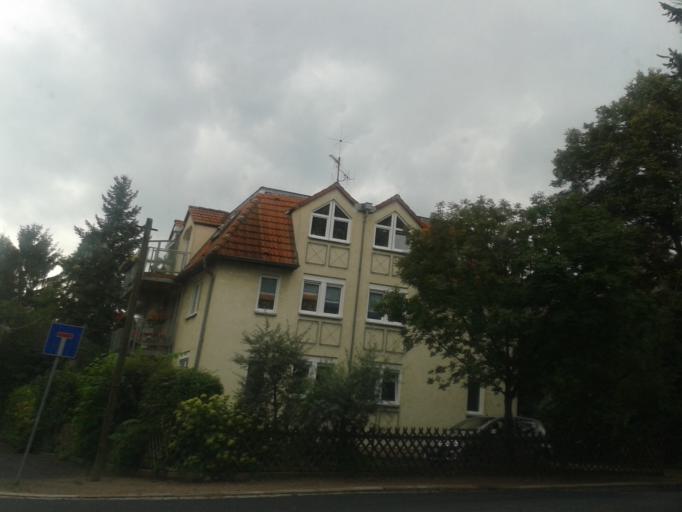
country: DE
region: Saxony
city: Radebeul
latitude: 51.1070
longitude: 13.6644
